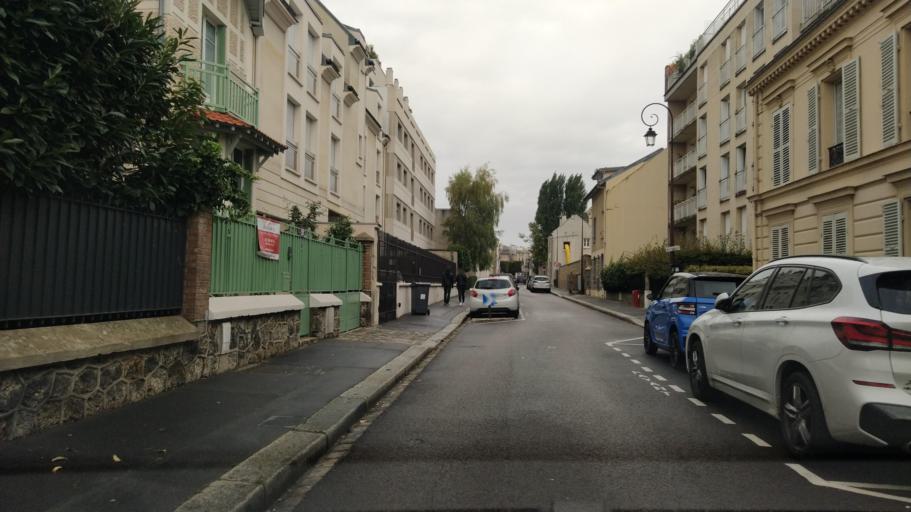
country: FR
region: Ile-de-France
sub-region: Departement des Yvelines
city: Versailles
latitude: 48.8126
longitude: 2.1320
